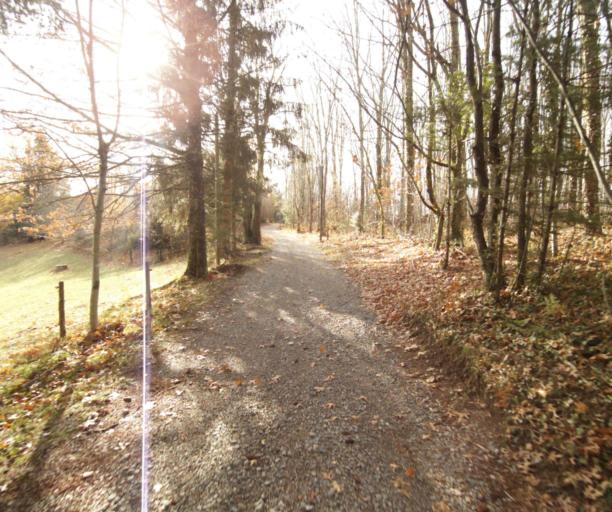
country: FR
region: Limousin
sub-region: Departement de la Correze
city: Sainte-Fortunade
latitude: 45.2019
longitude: 1.7371
